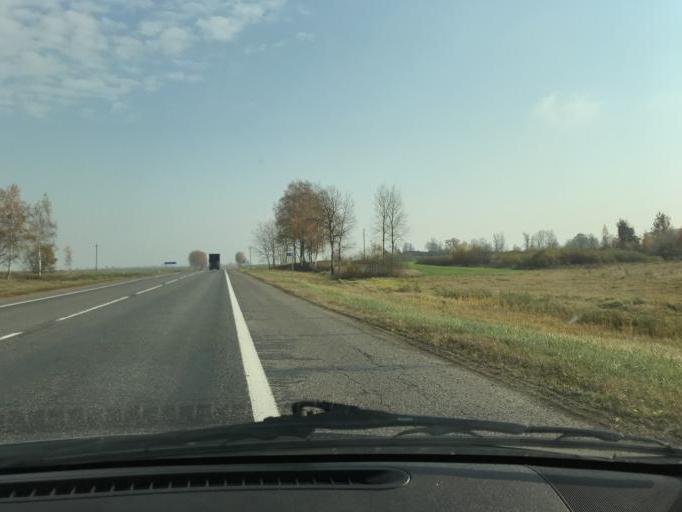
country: BY
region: Vitebsk
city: Chashniki
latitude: 55.0134
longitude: 29.1008
